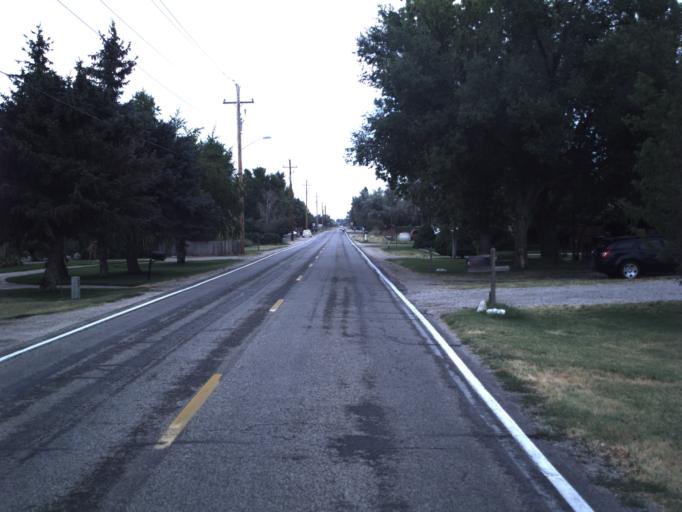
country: US
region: Utah
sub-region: Davis County
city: West Point
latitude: 41.1277
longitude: -112.1126
